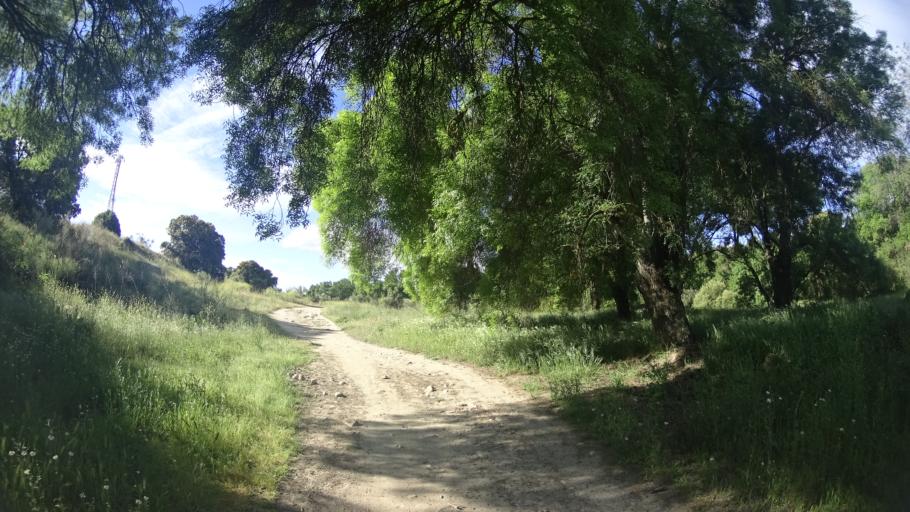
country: ES
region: Madrid
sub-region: Provincia de Madrid
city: Villanueva del Pardillo
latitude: 40.5160
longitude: -3.9415
